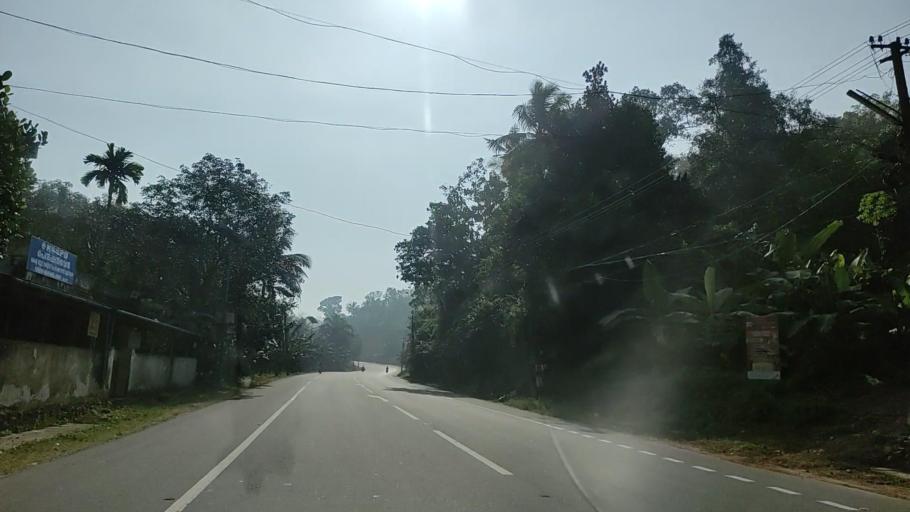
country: IN
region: Kerala
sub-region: Kollam
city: Punalur
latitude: 8.9684
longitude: 76.8305
